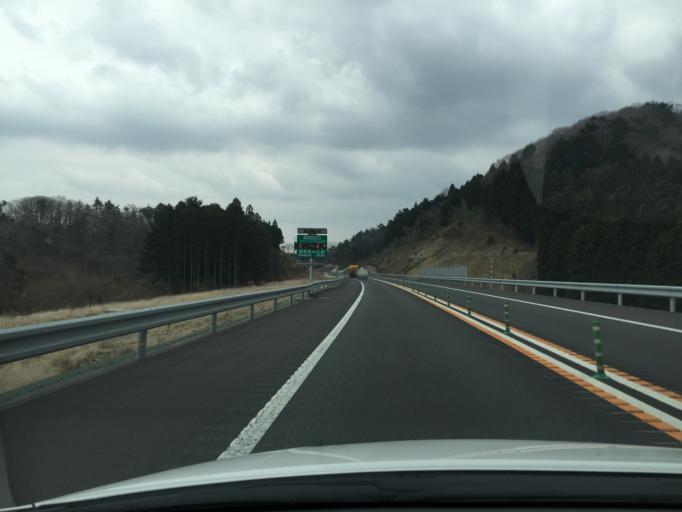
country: JP
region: Miyagi
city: Marumori
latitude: 37.8197
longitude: 140.8752
